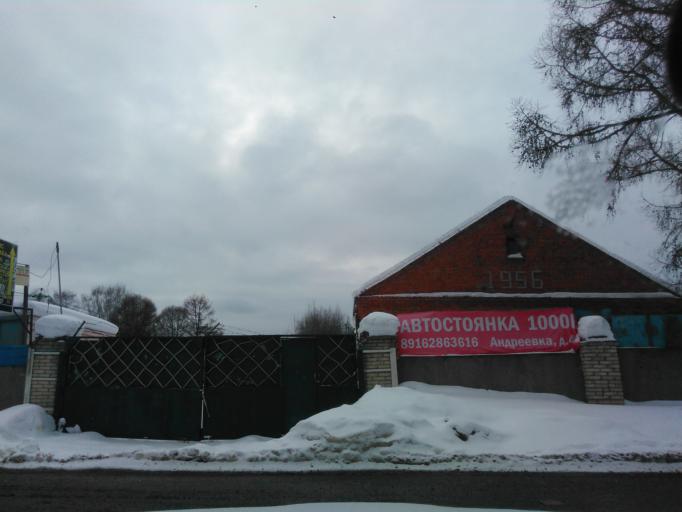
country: RU
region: Moskovskaya
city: Andreyevka
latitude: 55.9764
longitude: 37.1332
